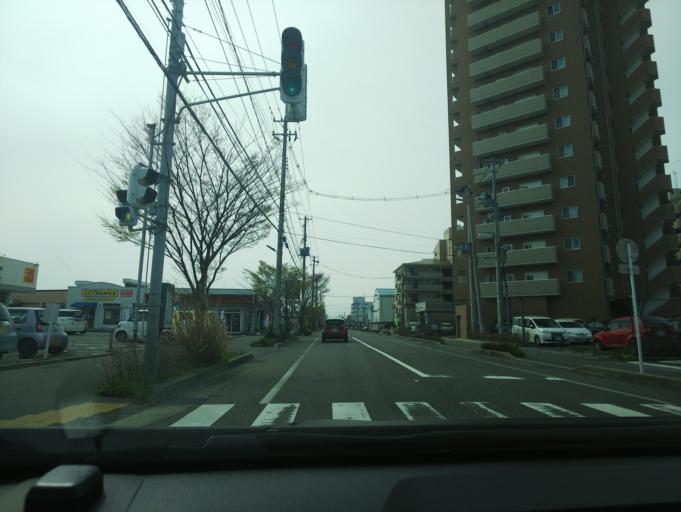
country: JP
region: Niigata
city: Niigata-shi
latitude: 37.9085
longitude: 139.0691
